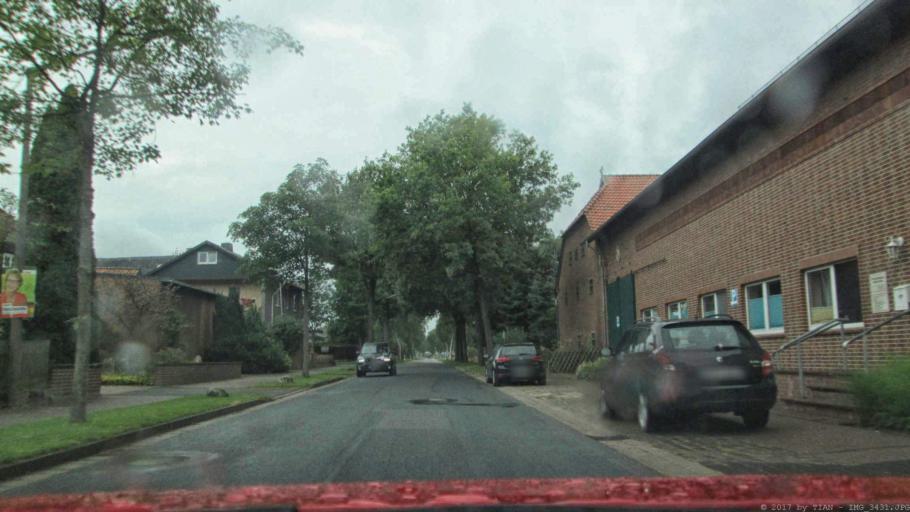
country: DE
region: Lower Saxony
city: Wahrenholz
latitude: 52.6158
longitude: 10.5966
